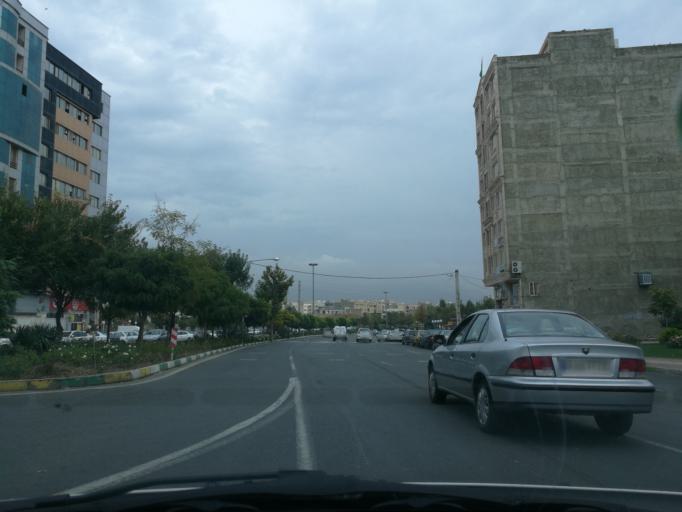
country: IR
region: Alborz
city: Karaj
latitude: 35.8521
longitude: 50.9643
